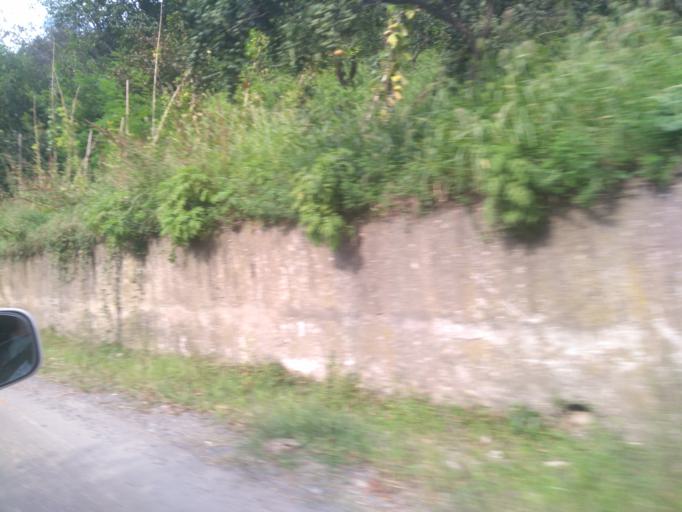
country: GE
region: Ajaria
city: Khelvachauri
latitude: 41.5644
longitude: 41.6921
